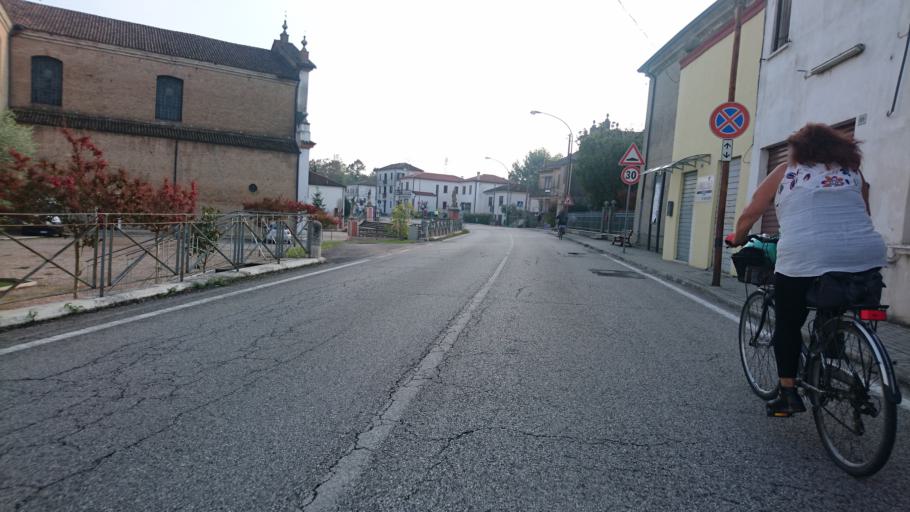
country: IT
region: Veneto
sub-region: Provincia di Rovigo
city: Polesella
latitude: 44.9660
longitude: 11.7499
